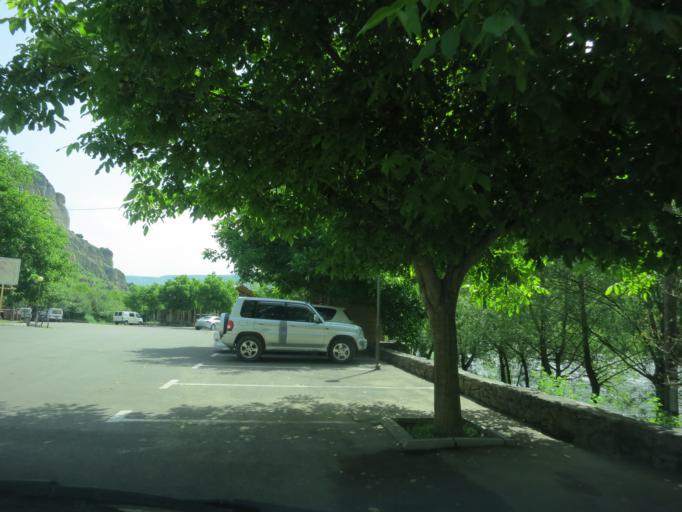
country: TR
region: Ardahan
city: Kurtkale
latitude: 41.3783
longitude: 43.2829
